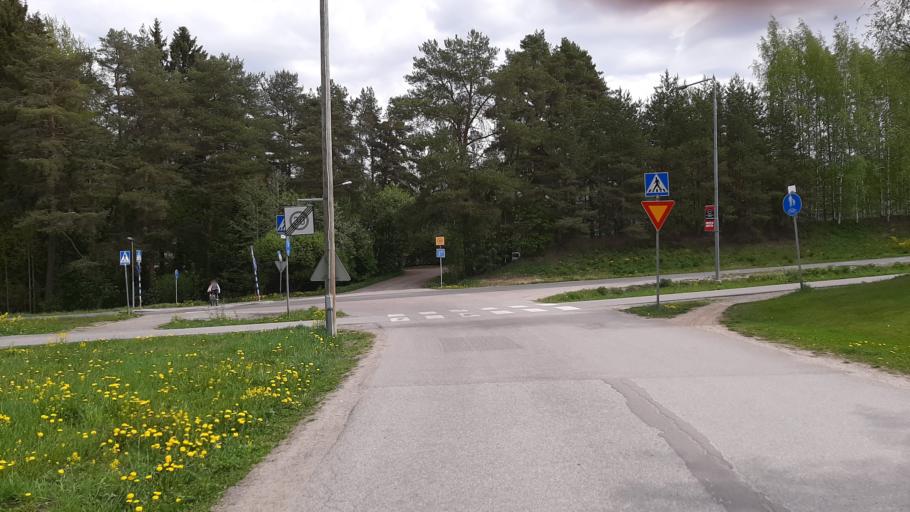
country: FI
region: Pirkanmaa
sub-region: Tampere
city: Tampere
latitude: 61.4749
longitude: 23.8590
